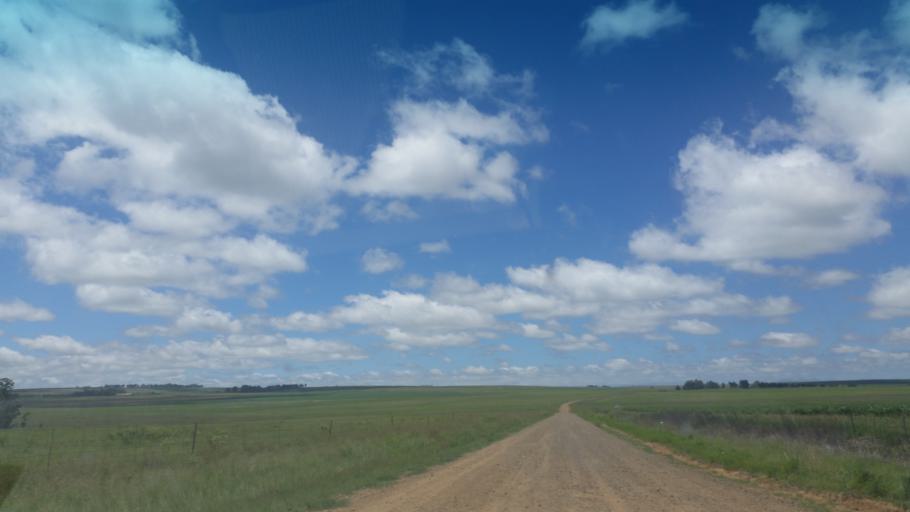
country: ZA
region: Orange Free State
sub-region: Thabo Mofutsanyana District Municipality
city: Harrismith
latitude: -28.1705
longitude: 29.0112
